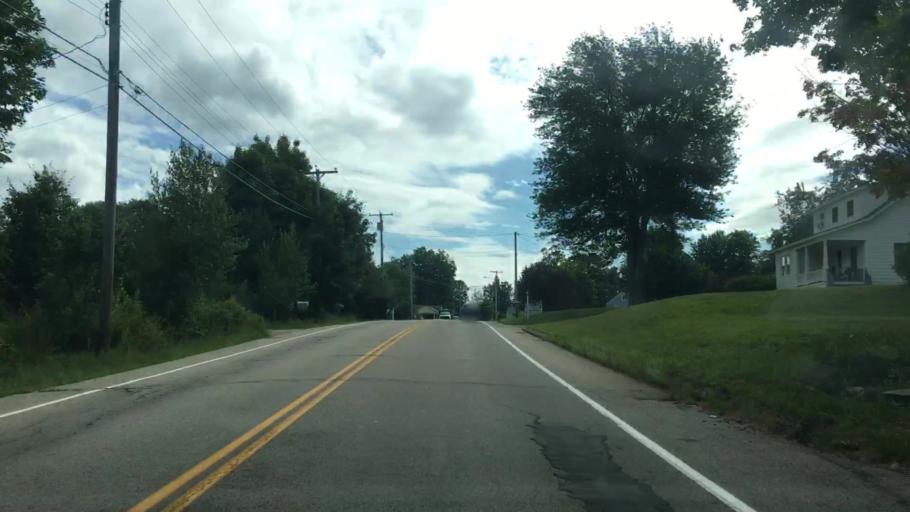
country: US
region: Maine
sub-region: York County
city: North Berwick
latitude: 43.2898
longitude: -70.7875
